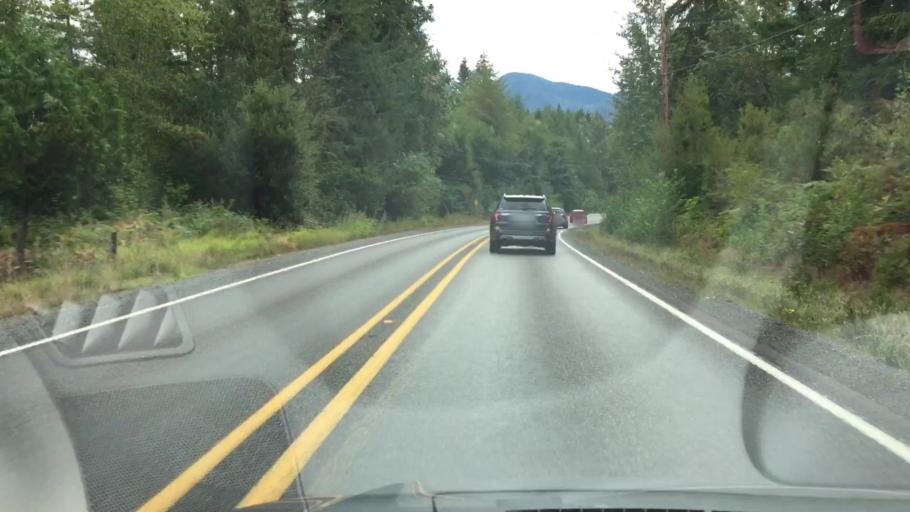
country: US
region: Washington
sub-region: Pierce County
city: Eatonville
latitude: 46.8075
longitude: -122.2666
